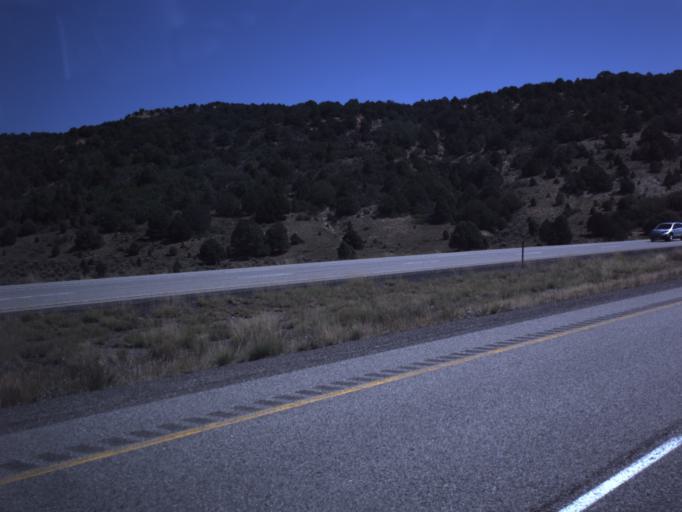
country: US
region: Utah
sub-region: Wayne County
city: Loa
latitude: 38.7777
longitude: -111.4805
